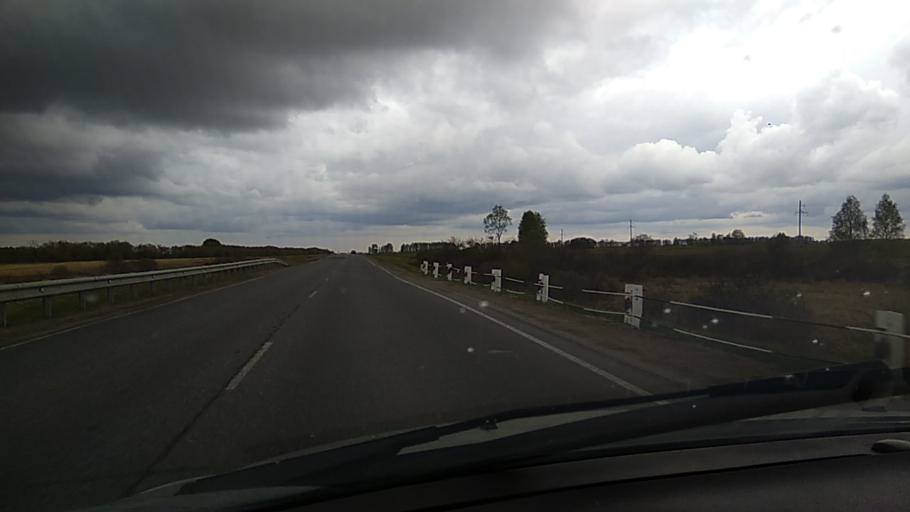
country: RU
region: Kurgan
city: Dalmatovo
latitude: 56.2897
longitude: 62.8431
